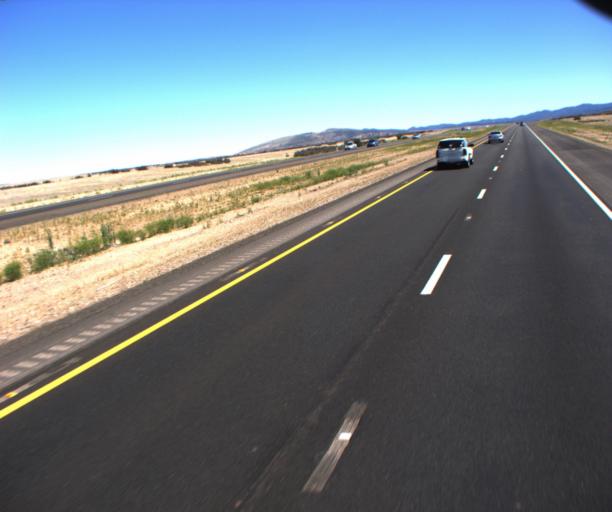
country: US
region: Arizona
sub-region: Yavapai County
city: Chino Valley
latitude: 34.6712
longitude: -112.4404
